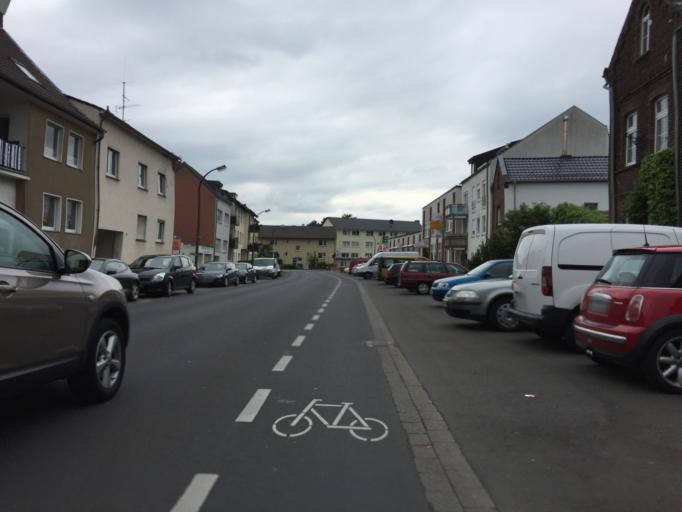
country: DE
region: North Rhine-Westphalia
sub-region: Regierungsbezirk Koln
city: Bonn
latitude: 50.7132
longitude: 7.0713
